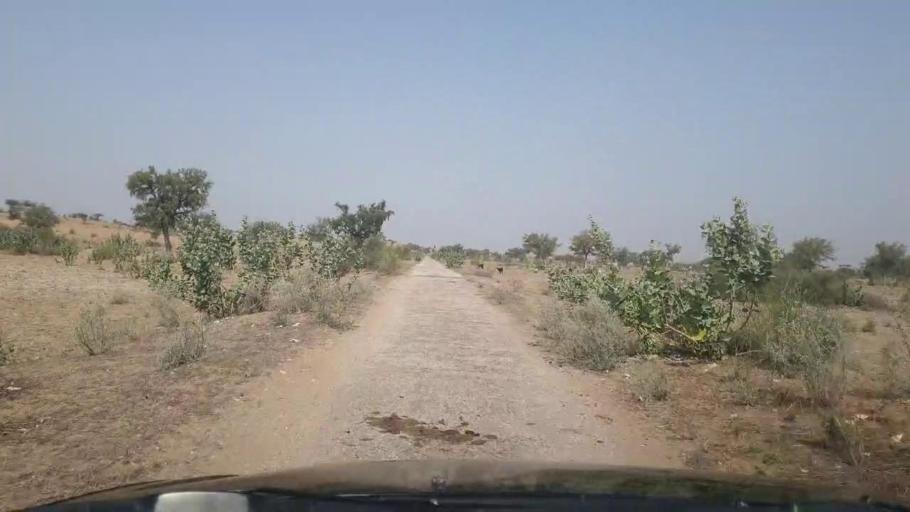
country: PK
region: Sindh
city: Islamkot
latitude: 25.0607
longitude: 70.2072
